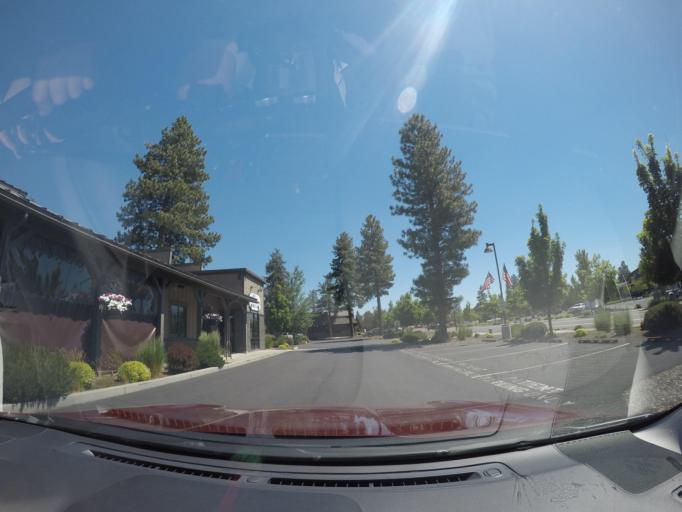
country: US
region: Oregon
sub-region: Deschutes County
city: Sisters
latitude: 44.2969
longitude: -121.5613
